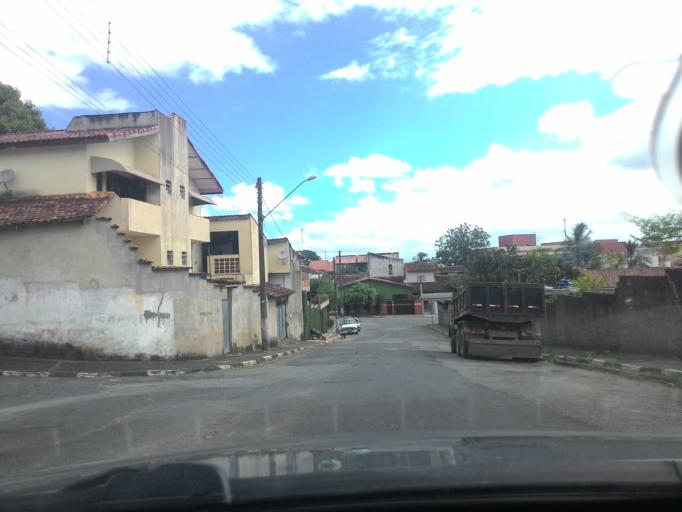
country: BR
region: Sao Paulo
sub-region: Registro
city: Registro
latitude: -24.4985
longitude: -47.8387
